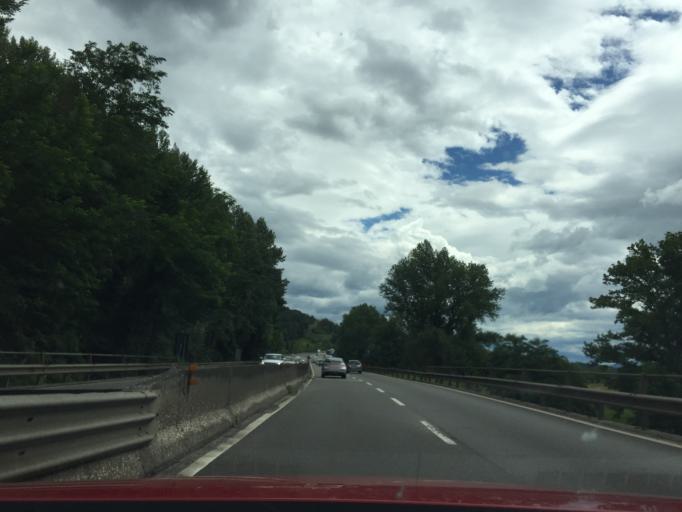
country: IT
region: Tuscany
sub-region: Province of Florence
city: Ginestra Fiorentina
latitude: 43.7114
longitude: 11.0533
